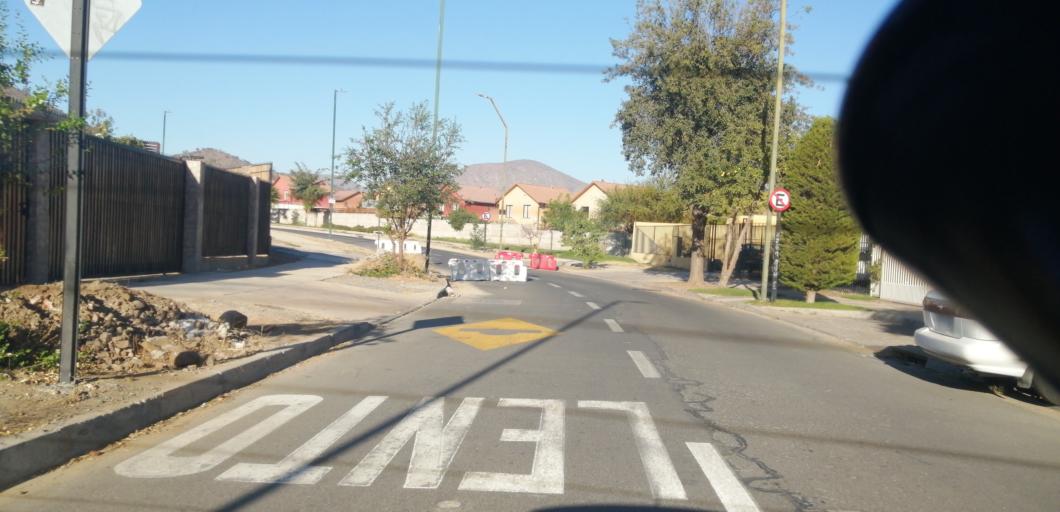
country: CL
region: Santiago Metropolitan
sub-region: Provincia de Santiago
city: Lo Prado
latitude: -33.4521
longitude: -70.8446
